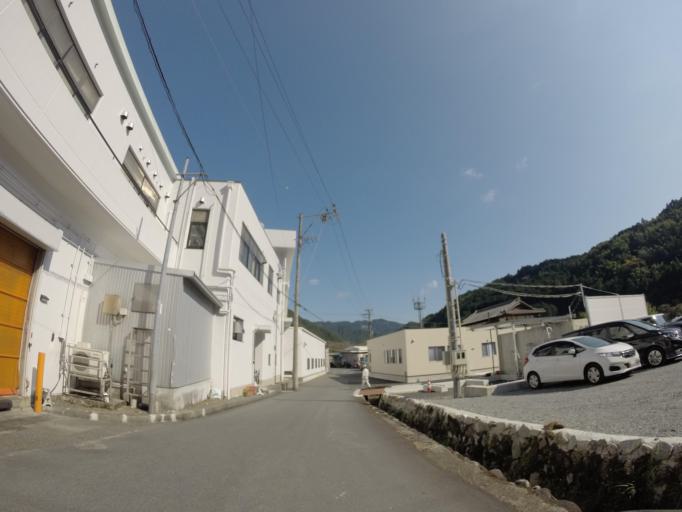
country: JP
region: Shizuoka
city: Shizuoka-shi
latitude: 35.1073
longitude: 138.4638
